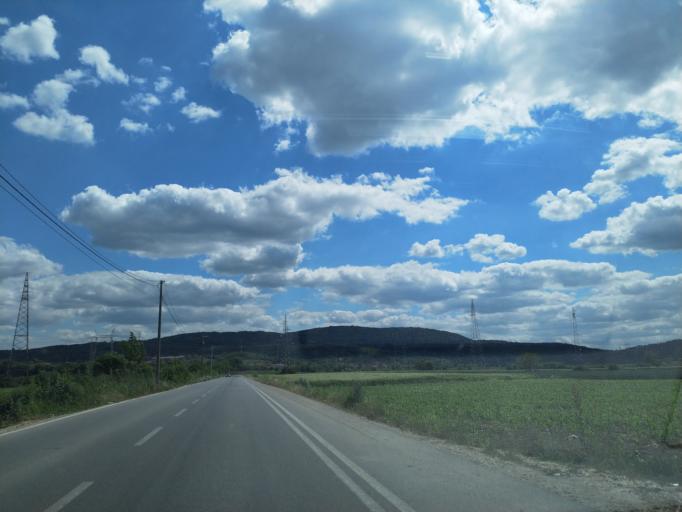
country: RS
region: Central Serbia
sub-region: Pomoravski Okrug
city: Jagodina
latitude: 43.9567
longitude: 21.2911
